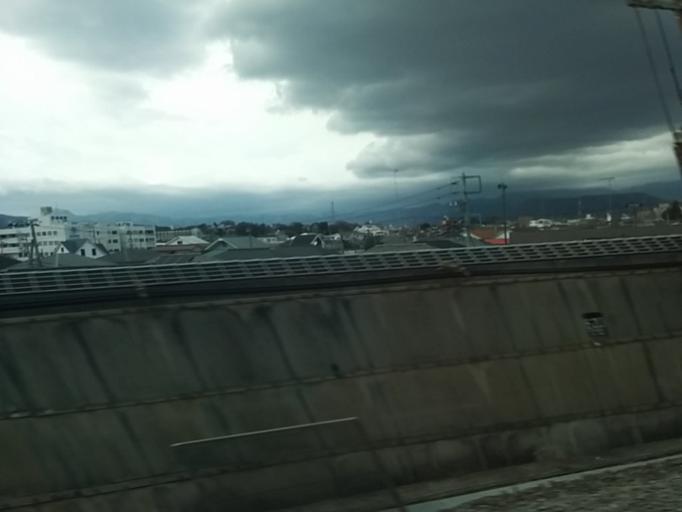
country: JP
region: Kanagawa
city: Odawara
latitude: 35.2638
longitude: 139.1621
